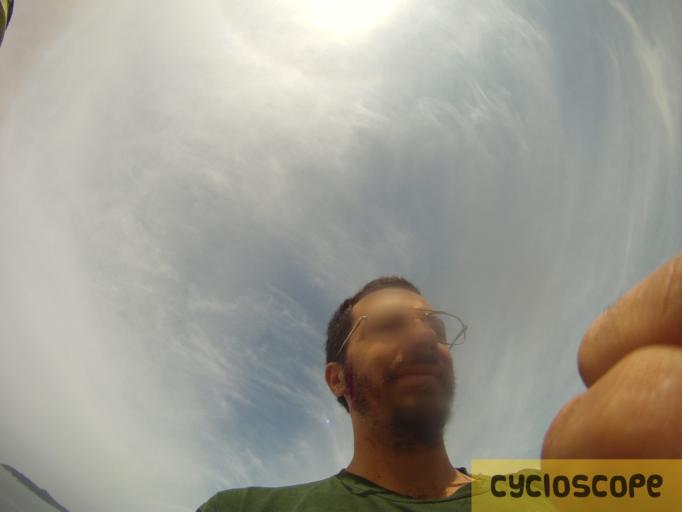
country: KR
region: Chungcheongnam-do
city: Taesal-li
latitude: 37.2810
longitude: 126.4257
